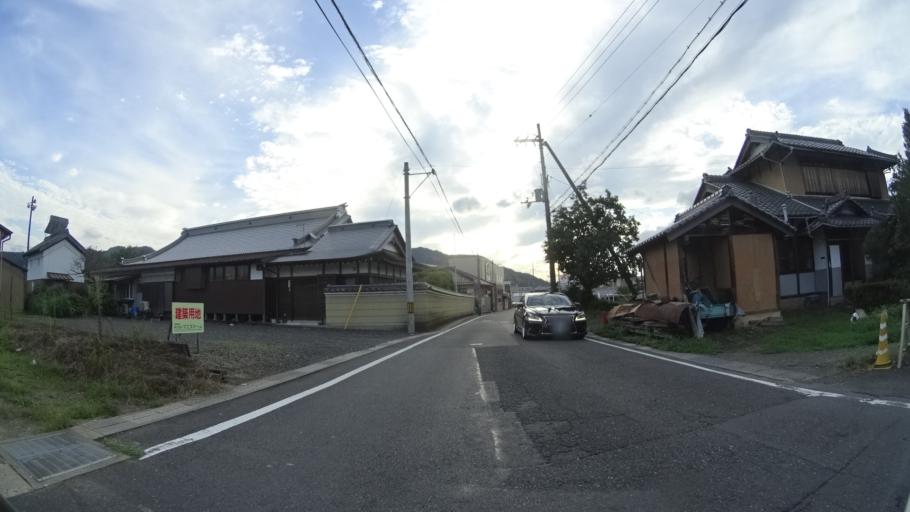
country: JP
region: Kyoto
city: Maizuru
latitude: 35.4267
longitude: 135.3322
